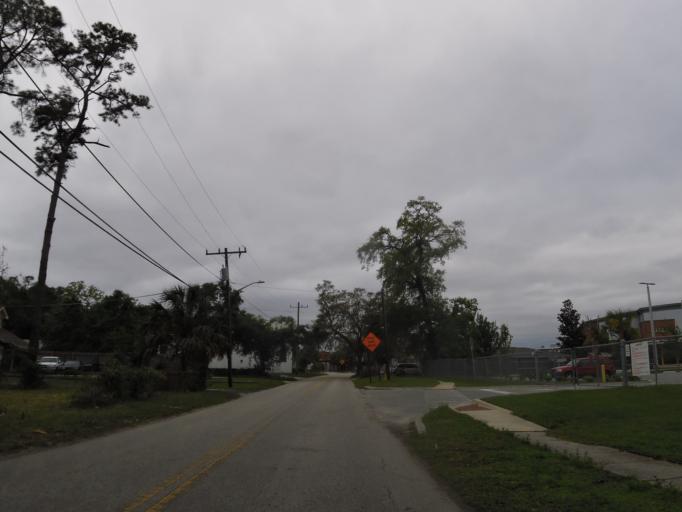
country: US
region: Florida
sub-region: Duval County
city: Jacksonville
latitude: 30.2995
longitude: -81.6366
